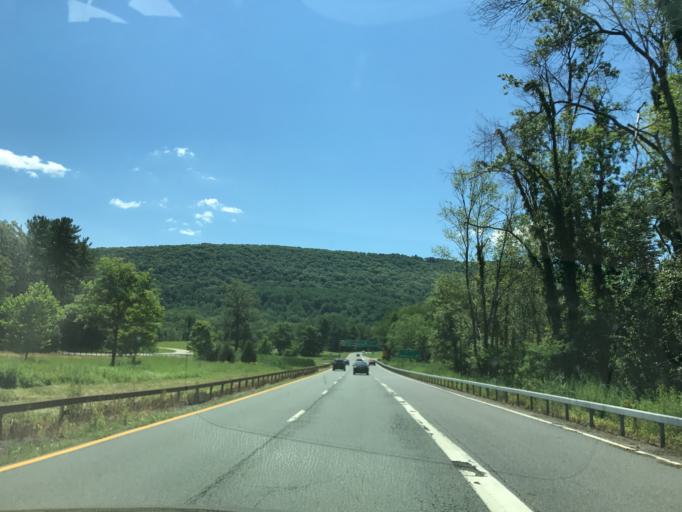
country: US
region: New York
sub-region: Dutchess County
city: Hillside Lake
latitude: 41.5441
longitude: -73.7751
